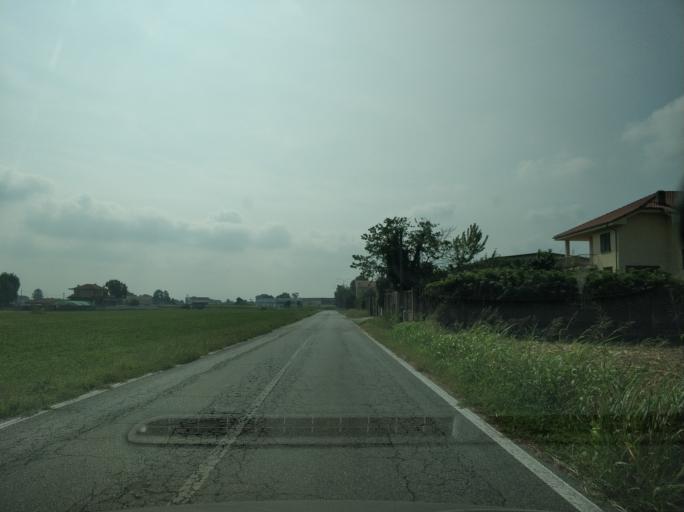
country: IT
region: Piedmont
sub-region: Provincia di Torino
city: San Maurizio
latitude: 45.1968
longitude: 7.6209
